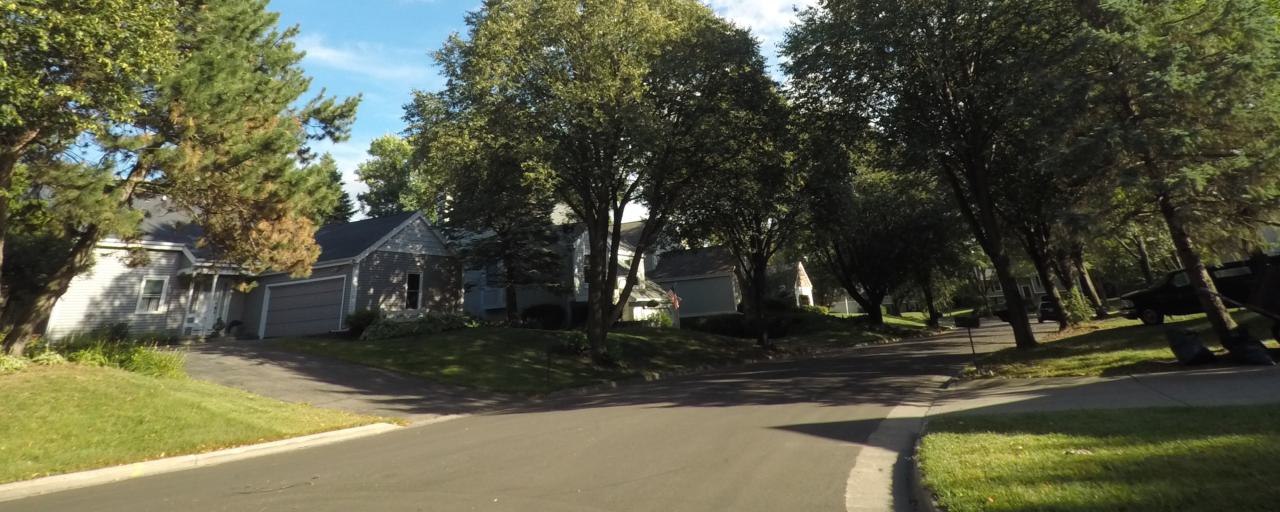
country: US
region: Wisconsin
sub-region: Dane County
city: Middleton
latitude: 43.0655
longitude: -89.5194
